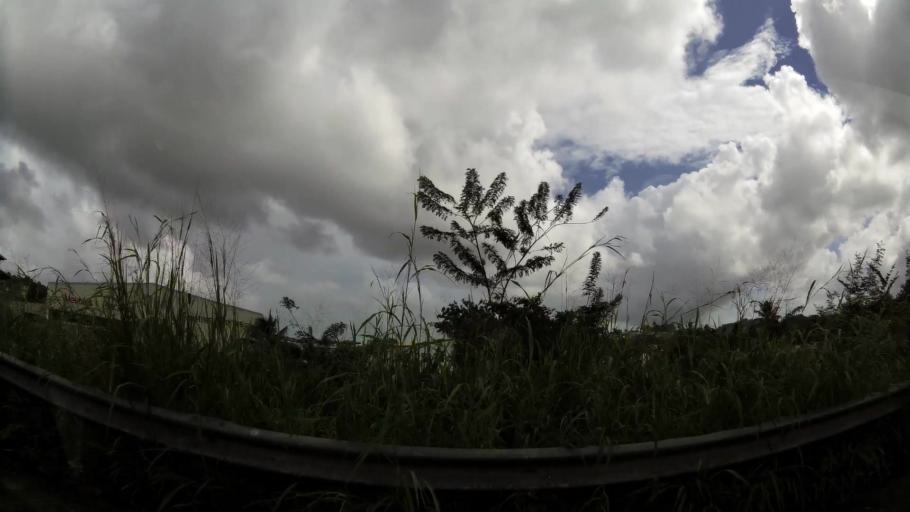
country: MQ
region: Martinique
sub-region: Martinique
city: Ducos
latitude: 14.5698
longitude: -60.9801
